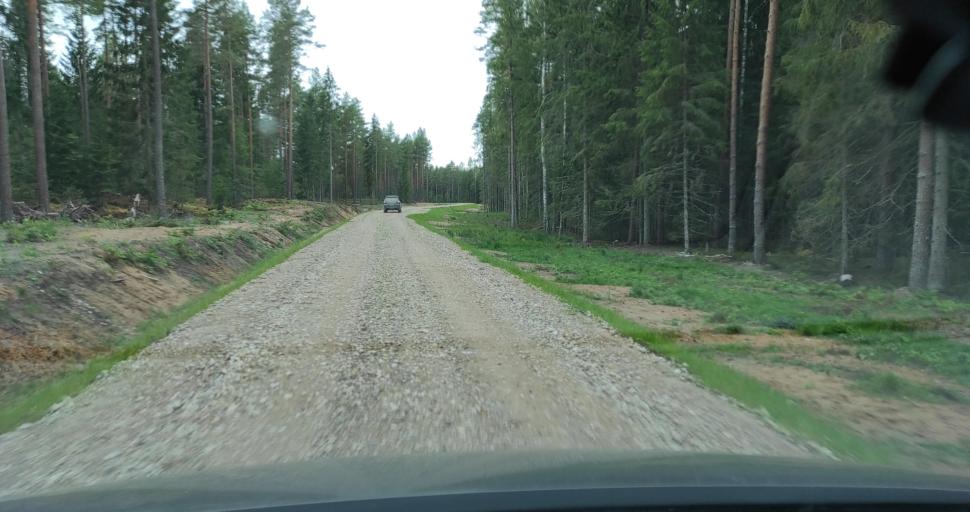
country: LV
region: Kuldigas Rajons
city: Kuldiga
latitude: 57.0812
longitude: 22.2030
